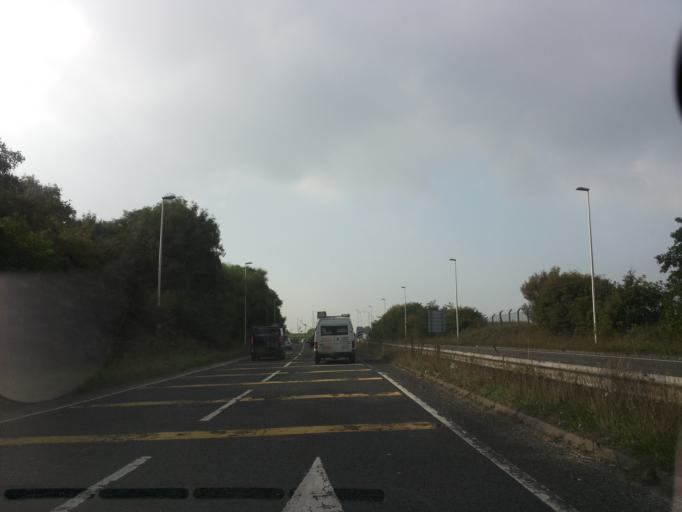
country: GB
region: England
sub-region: Lancashire
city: Great Marton
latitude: 53.7943
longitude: -2.9980
